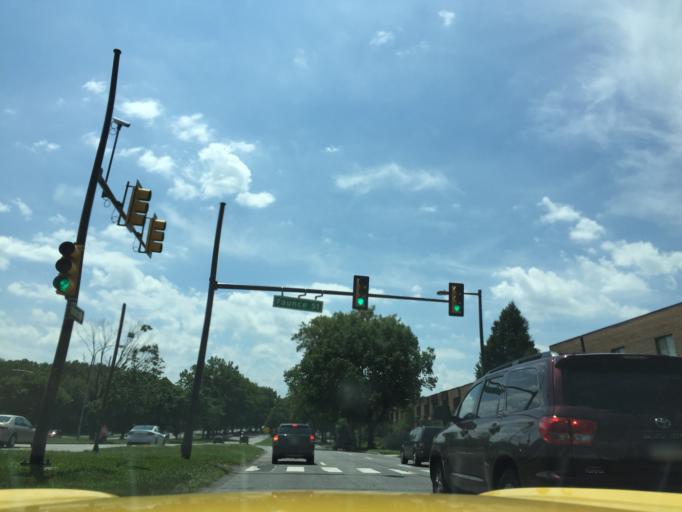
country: US
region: Pennsylvania
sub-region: Montgomery County
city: Rockledge
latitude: 40.0507
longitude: -75.0514
